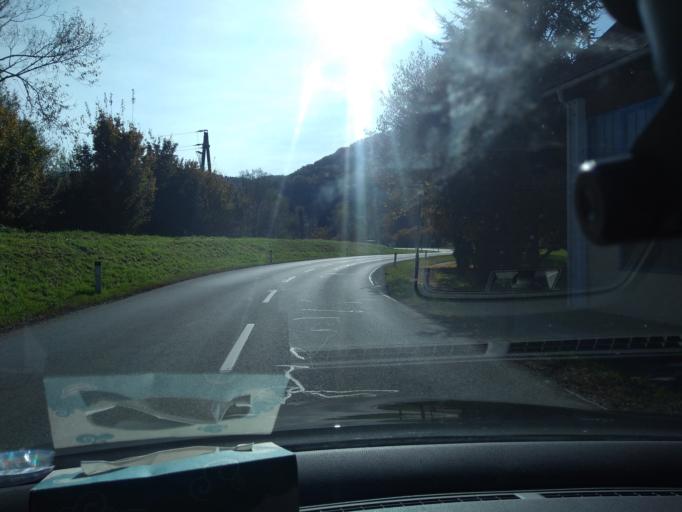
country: AT
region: Styria
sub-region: Politischer Bezirk Leibnitz
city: Wildon
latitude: 46.8911
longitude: 15.5186
